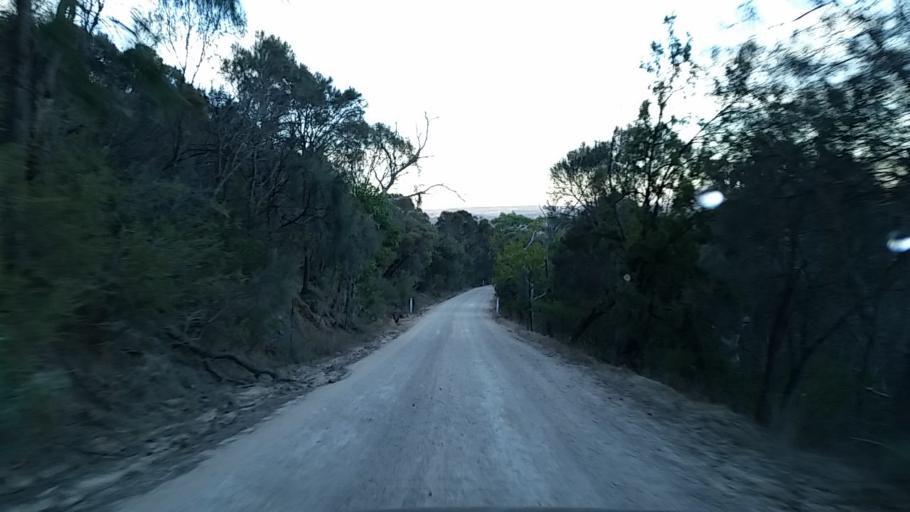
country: AU
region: South Australia
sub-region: Mount Barker
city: Nairne
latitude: -35.0647
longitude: 138.9235
